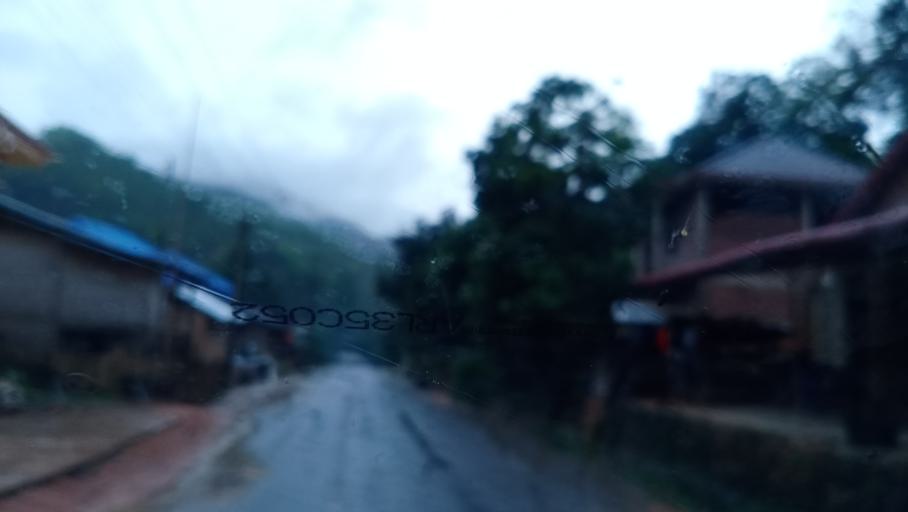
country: LA
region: Phongsali
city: Khoa
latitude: 21.0675
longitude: 102.4897
